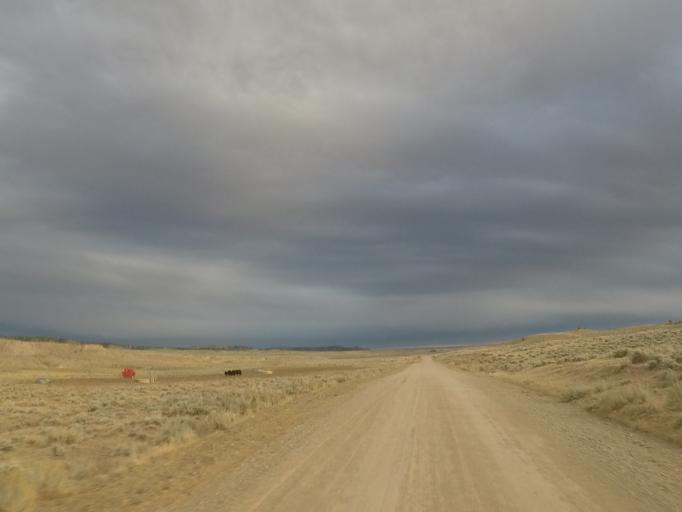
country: US
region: Montana
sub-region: Golden Valley County
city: Ryegate
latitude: 46.4332
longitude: -109.2550
